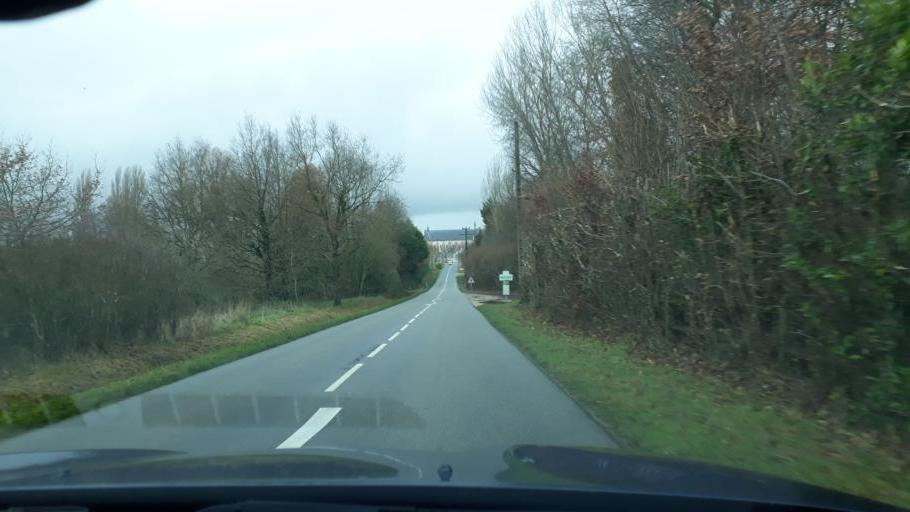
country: FR
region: Centre
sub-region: Departement du Loiret
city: Clery-Saint-Andre
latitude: 47.8147
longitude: 1.7592
